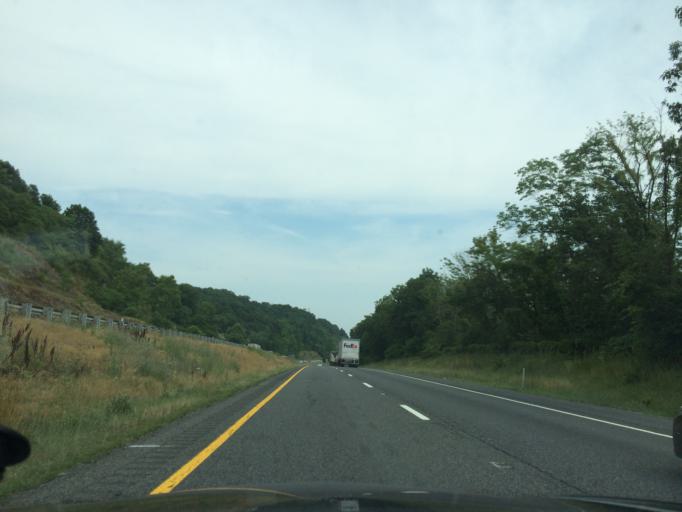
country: US
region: Maryland
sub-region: Washington County
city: Hancock
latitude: 39.6700
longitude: -78.0732
